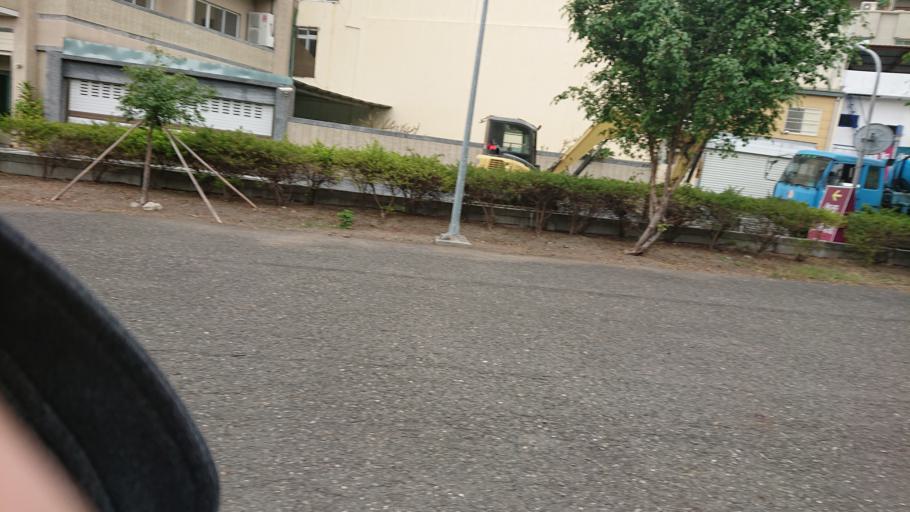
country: TW
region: Kaohsiung
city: Kaohsiung
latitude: 22.7050
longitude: 120.2930
